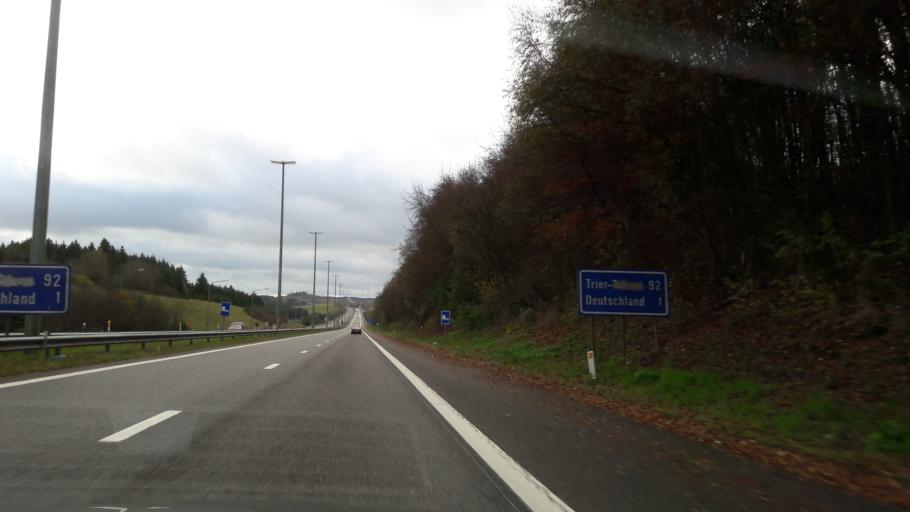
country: DE
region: Rheinland-Pfalz
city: Winterspelt
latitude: 50.2463
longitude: 6.1744
